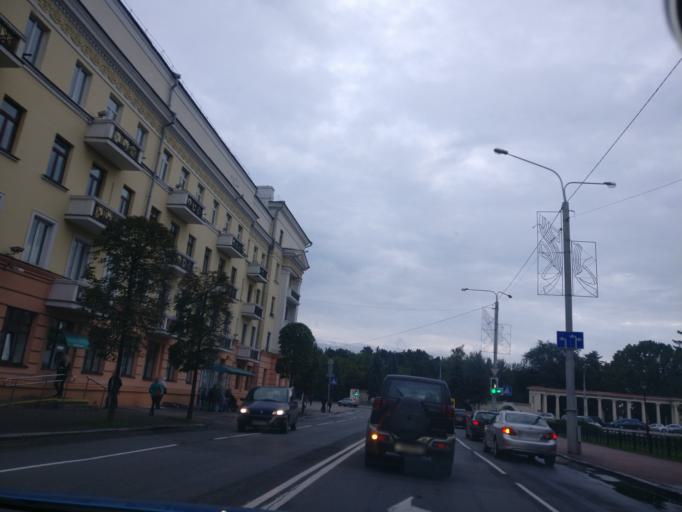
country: BY
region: Minsk
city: Minsk
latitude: 53.9240
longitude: 27.6085
